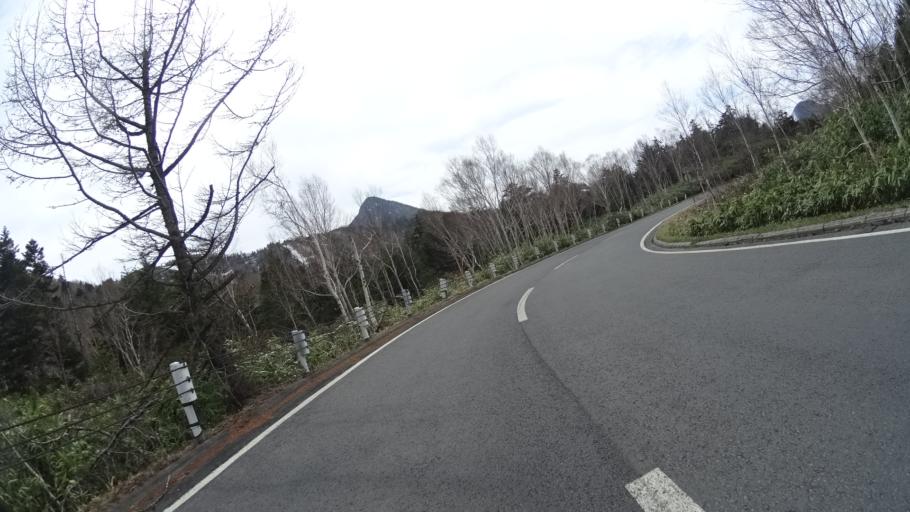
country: JP
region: Nagano
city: Nakano
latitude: 36.6811
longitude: 138.5019
